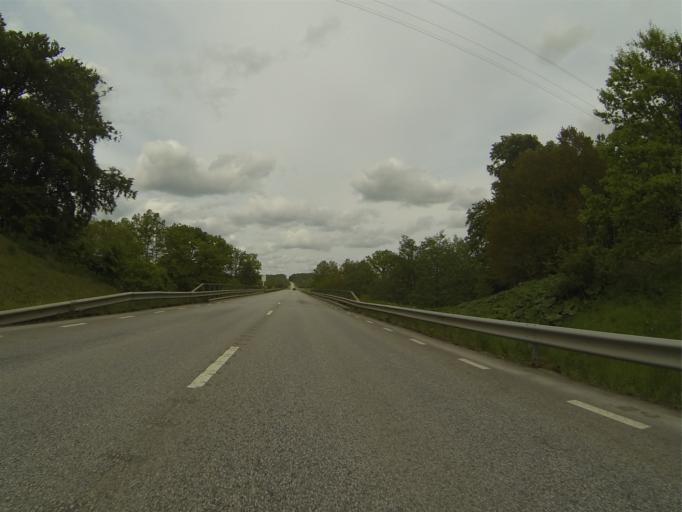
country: SE
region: Skane
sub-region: Sjobo Kommun
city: Sjoebo
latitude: 55.6468
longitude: 13.6917
